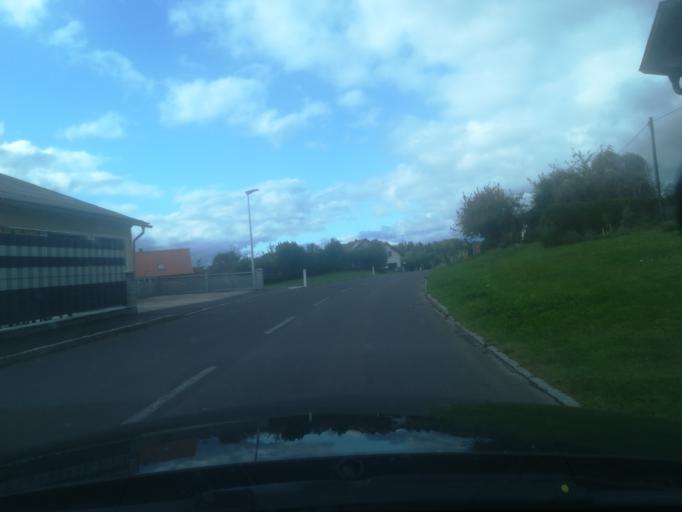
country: AT
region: Upper Austria
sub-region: Politischer Bezirk Urfahr-Umgebung
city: Herzogsdorf
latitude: 48.4280
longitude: 14.1282
